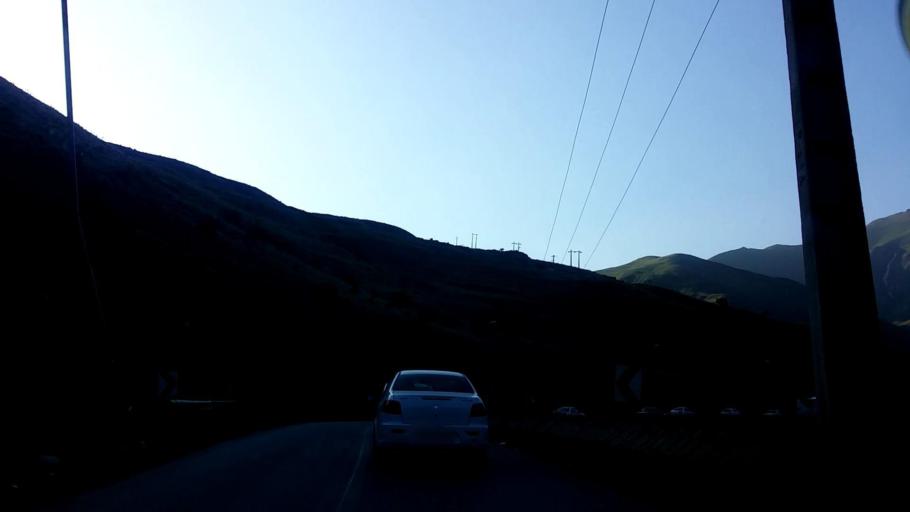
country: IR
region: Tehran
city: Tajrish
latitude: 36.1999
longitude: 51.3375
